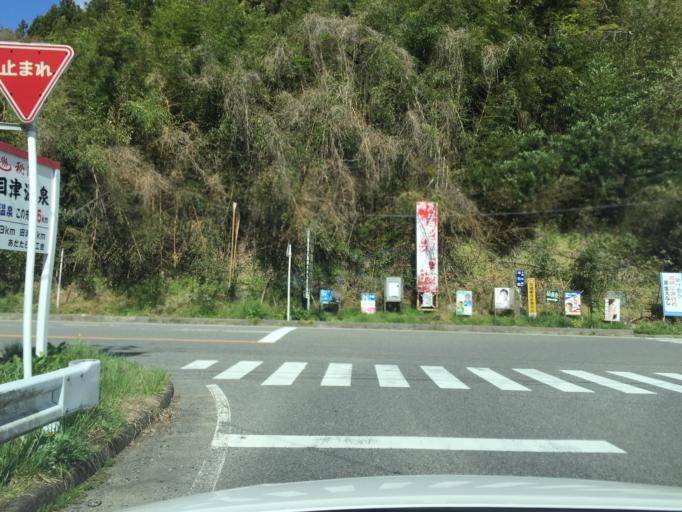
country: JP
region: Fukushima
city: Funehikimachi-funehiki
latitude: 37.5325
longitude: 140.5894
